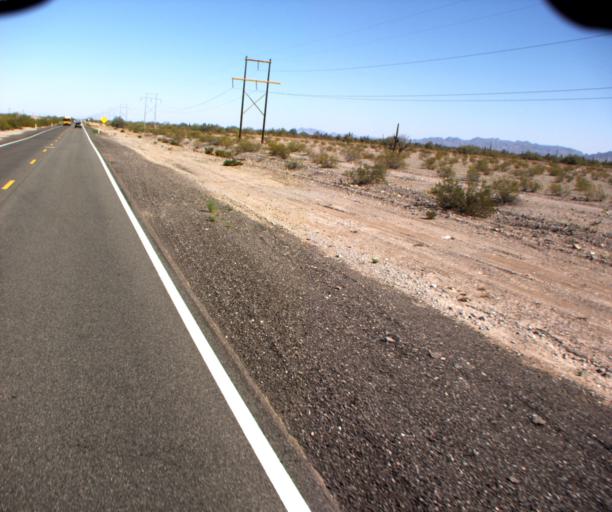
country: US
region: Arizona
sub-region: La Paz County
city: Quartzsite
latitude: 33.5728
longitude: -114.2170
